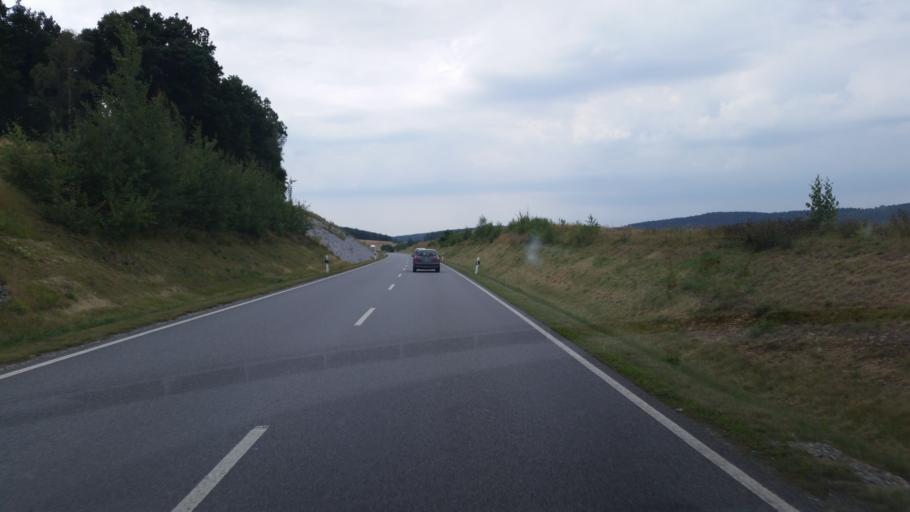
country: DE
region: Saxony
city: Elstra
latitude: 51.2052
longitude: 14.1507
